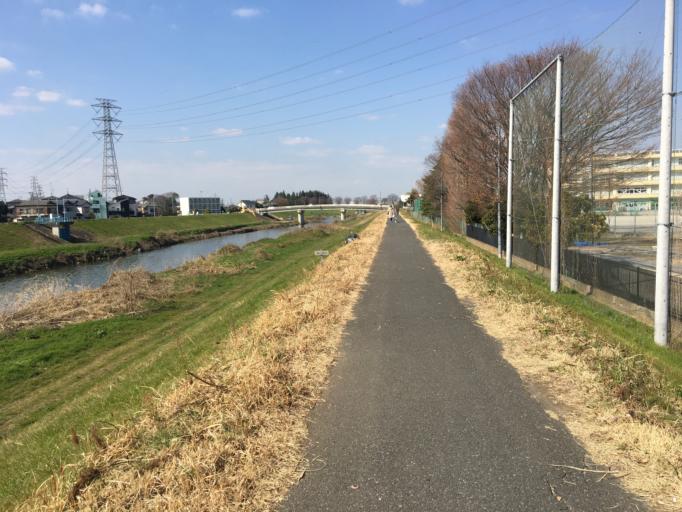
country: JP
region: Saitama
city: Shiki
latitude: 35.8413
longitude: 139.5794
